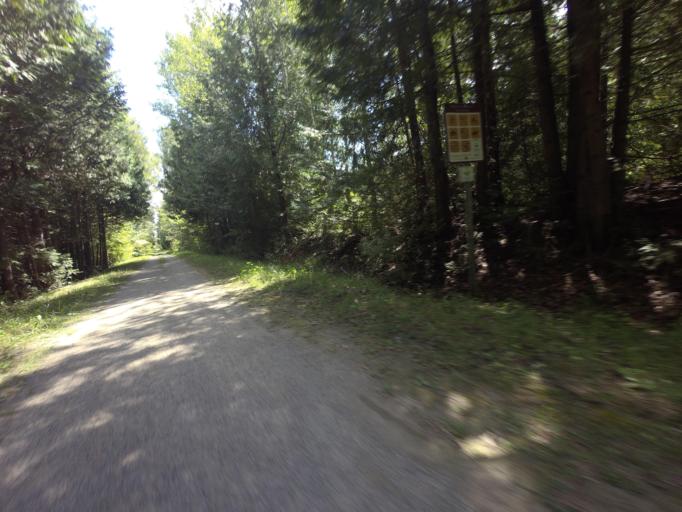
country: CA
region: Ontario
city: Orangeville
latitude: 43.7867
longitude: -80.2376
